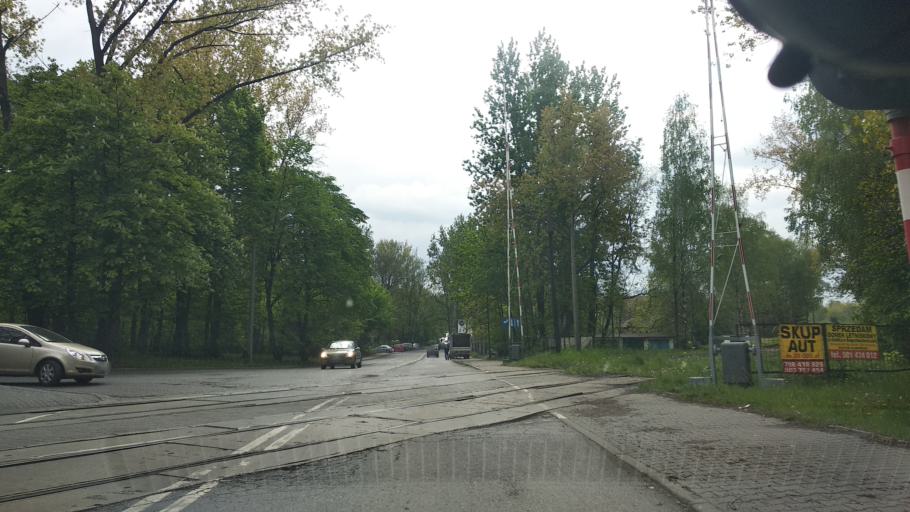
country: PL
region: Silesian Voivodeship
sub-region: Katowice
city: Katowice
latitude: 50.2429
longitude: 18.9824
